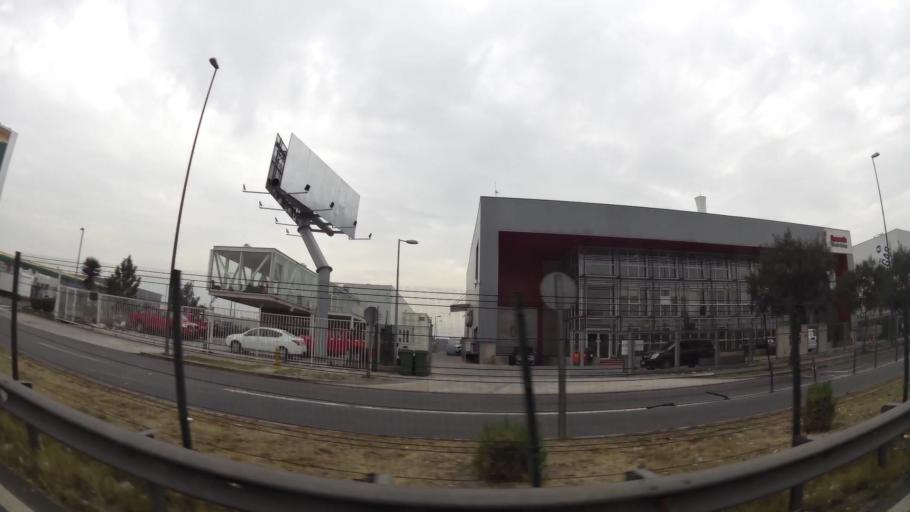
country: CL
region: Santiago Metropolitan
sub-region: Provincia de Santiago
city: Lo Prado
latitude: -33.4340
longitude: -70.7853
